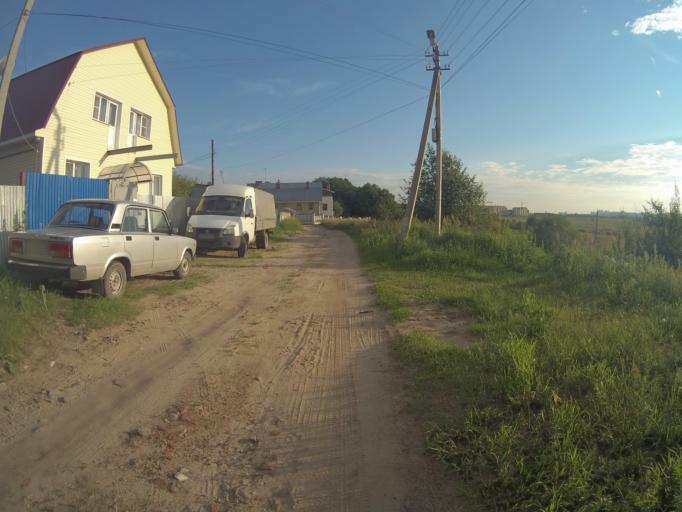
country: RU
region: Vladimir
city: Kommunar
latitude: 56.1172
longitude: 40.4514
